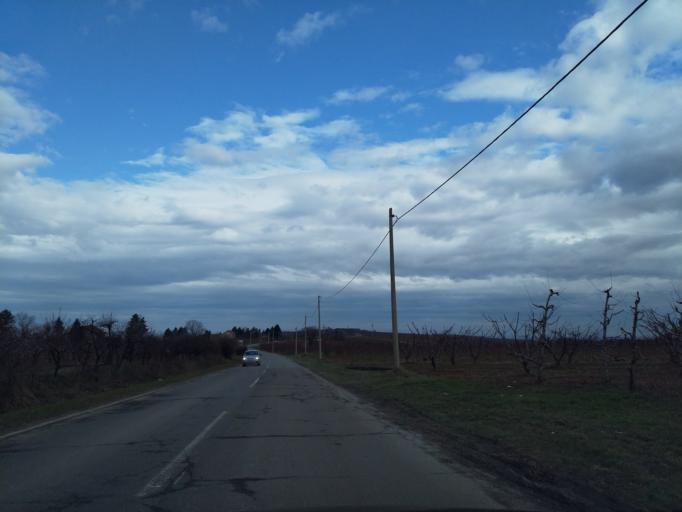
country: RS
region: Central Serbia
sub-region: Belgrade
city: Grocka
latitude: 44.6224
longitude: 20.7423
